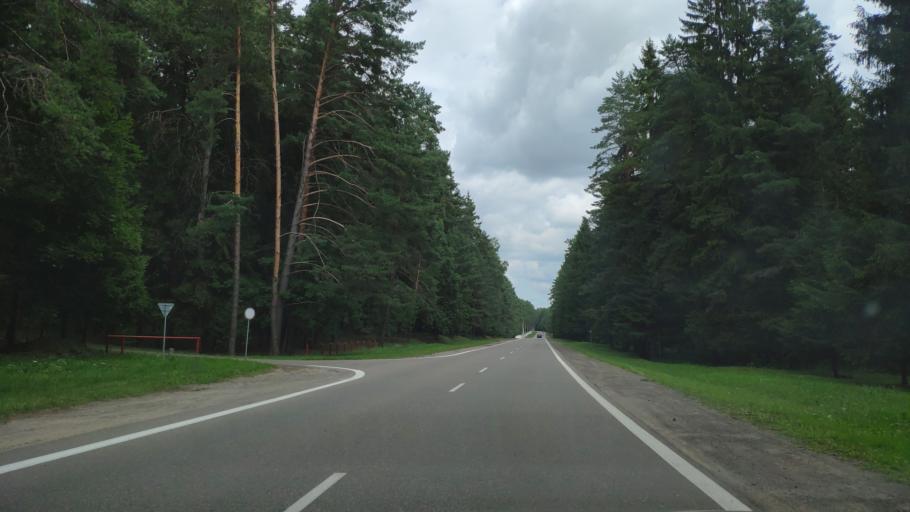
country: BY
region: Minsk
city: Syomkava
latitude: 53.9786
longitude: 27.4442
